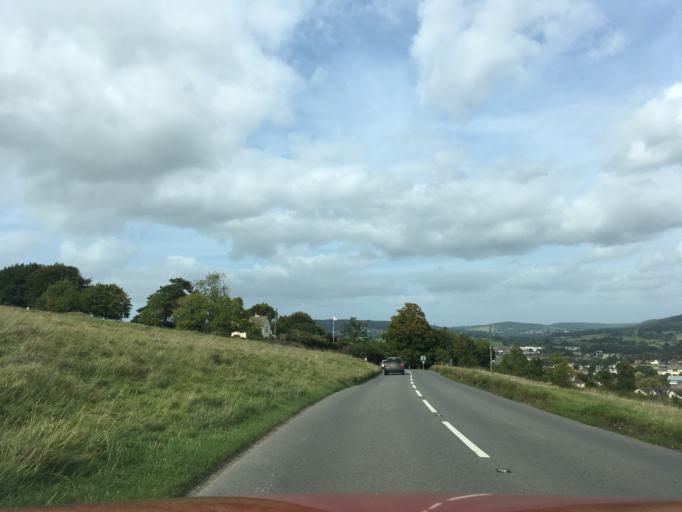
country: GB
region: England
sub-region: Gloucestershire
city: Nailsworth
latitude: 51.7300
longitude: -2.2431
